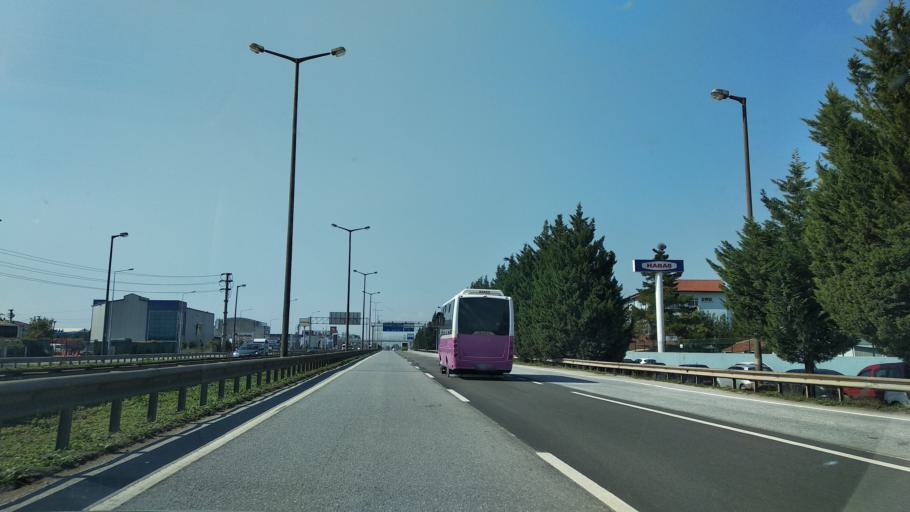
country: TR
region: Kocaeli
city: Kosekoy
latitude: 40.7519
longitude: 30.0339
